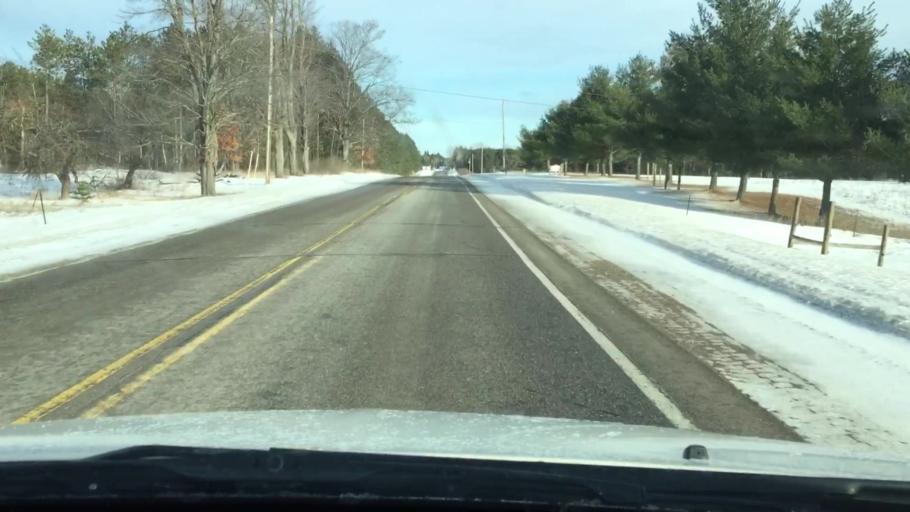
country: US
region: Michigan
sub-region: Kalkaska County
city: Kalkaska
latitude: 44.6406
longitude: -85.1856
